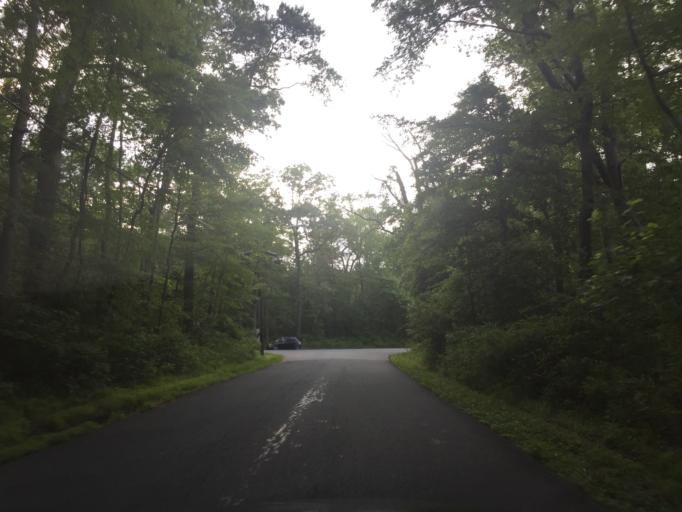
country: US
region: Maryland
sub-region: Baltimore County
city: Bowleys Quarters
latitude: 39.3048
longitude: -76.3755
